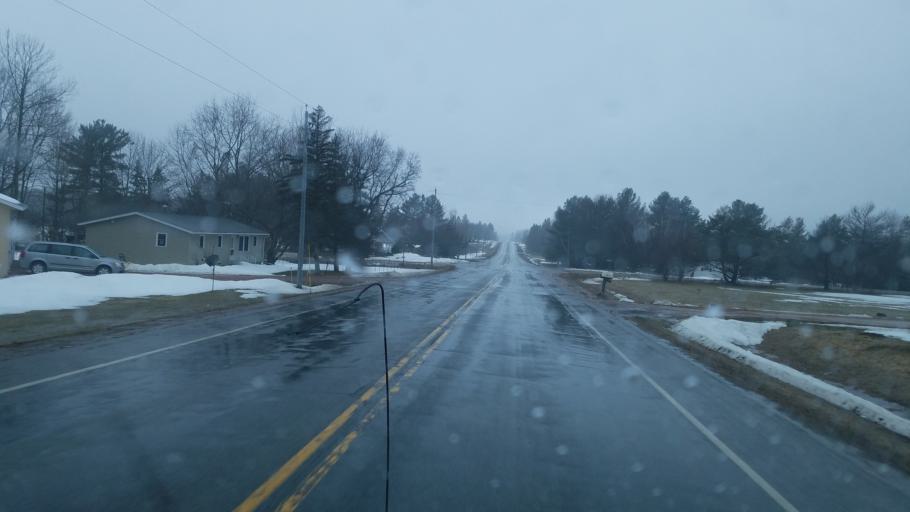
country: US
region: Wisconsin
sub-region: Wood County
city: Marshfield
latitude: 44.6779
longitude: -90.2573
